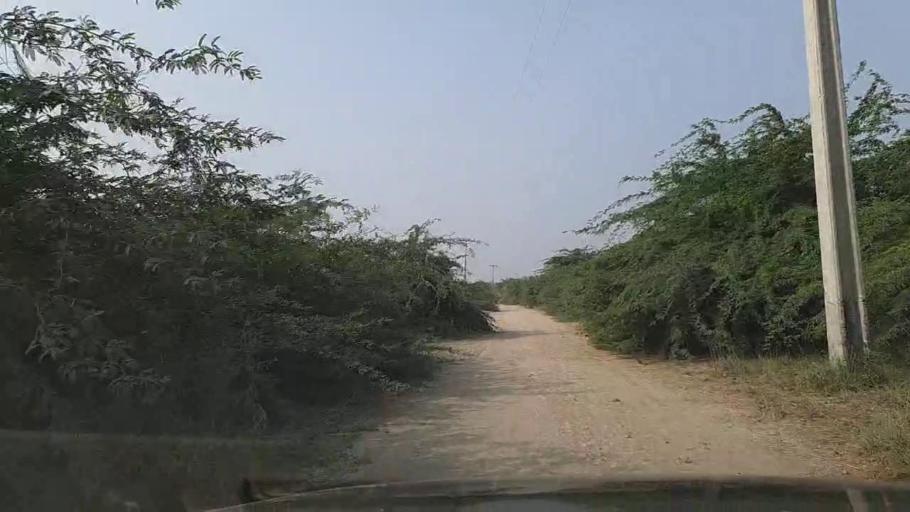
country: PK
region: Sindh
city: Thatta
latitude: 24.7659
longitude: 67.8481
